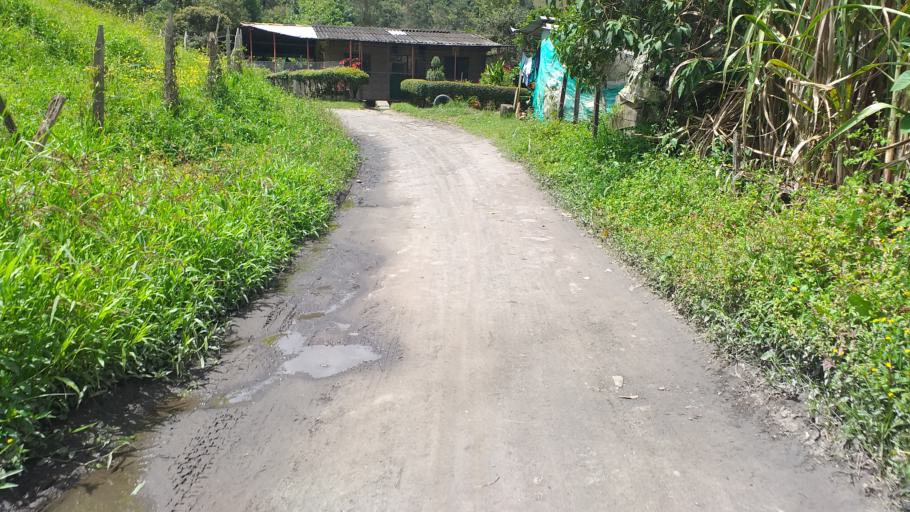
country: CO
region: Cundinamarca
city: Tenza
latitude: 5.1159
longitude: -73.4610
